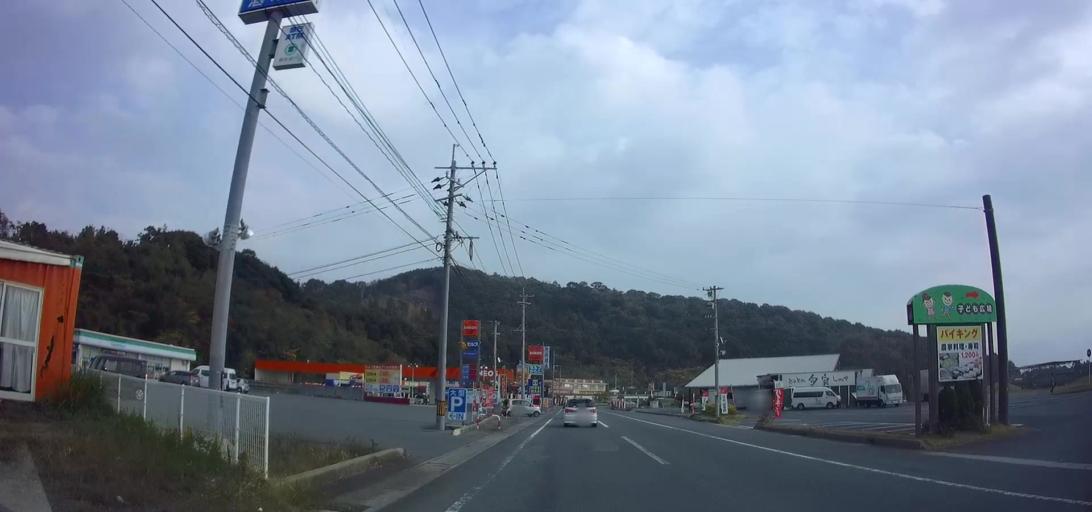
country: JP
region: Nagasaki
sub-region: Isahaya-shi
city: Isahaya
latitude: 32.7940
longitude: 130.1145
